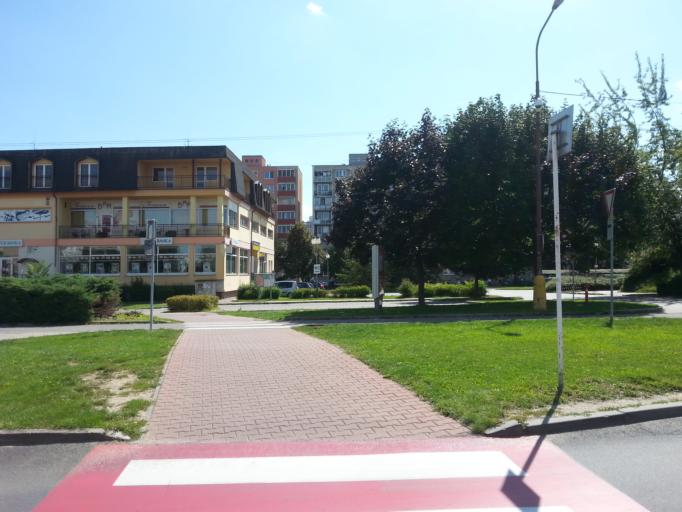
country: SK
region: Trenciansky
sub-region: Okres Nove Mesto nad Vahom
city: Nove Mesto nad Vahom
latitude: 48.7555
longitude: 17.8325
